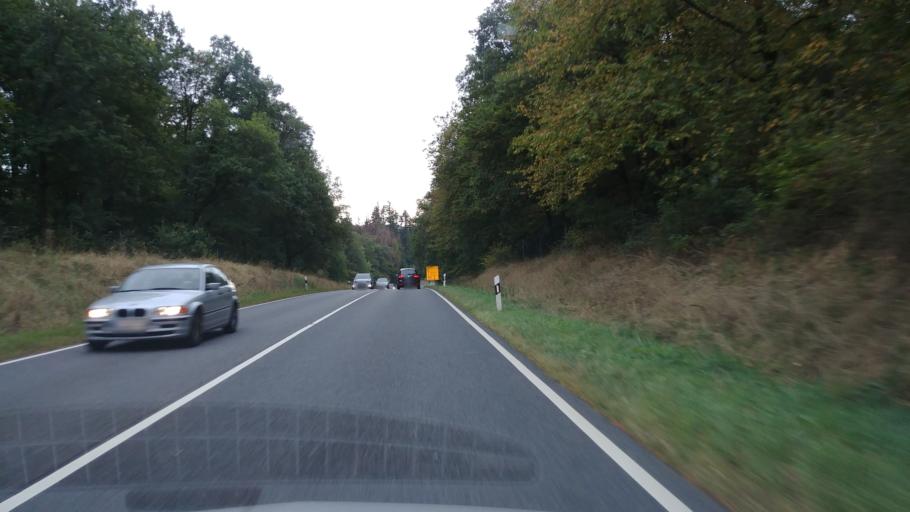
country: DE
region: Hesse
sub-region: Regierungsbezirk Darmstadt
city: Idstein
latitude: 50.2111
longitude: 8.2006
